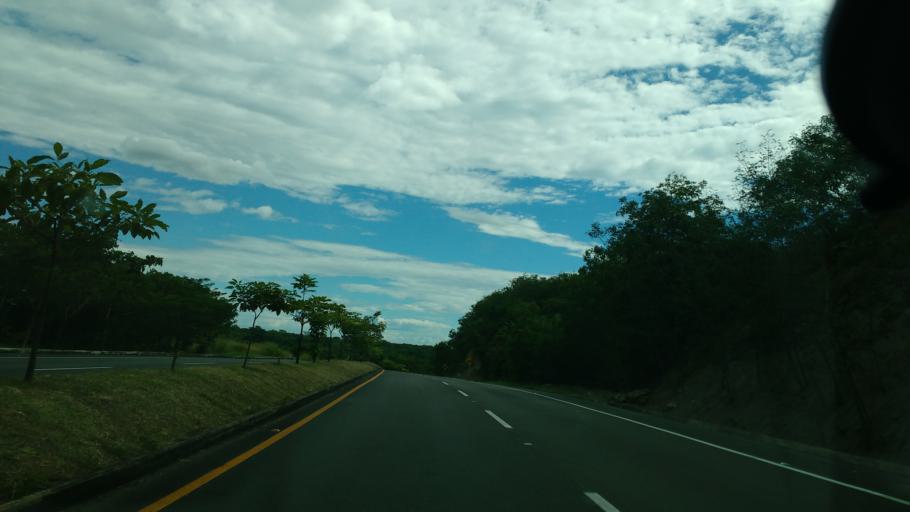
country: CO
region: Tolima
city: Espinal
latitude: 4.2148
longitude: -74.9533
